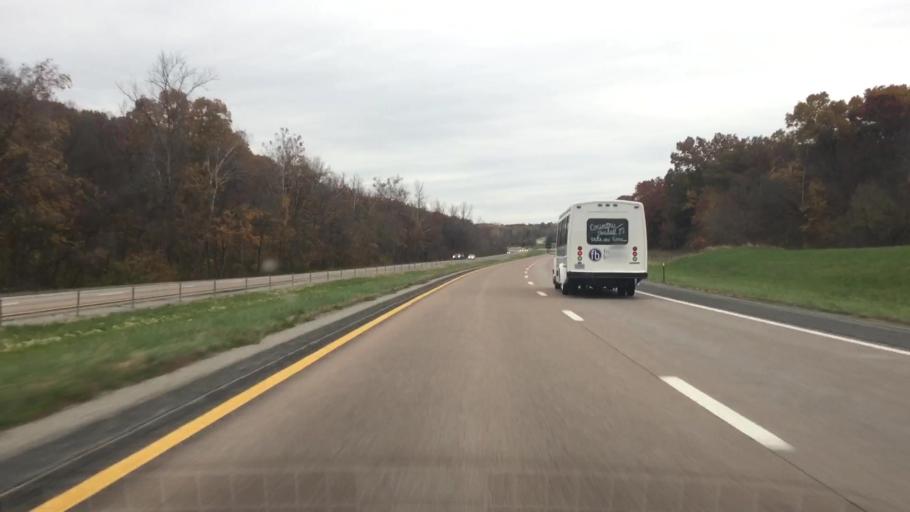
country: US
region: Missouri
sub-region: Cole County
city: Jefferson City
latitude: 38.6610
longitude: -92.2241
